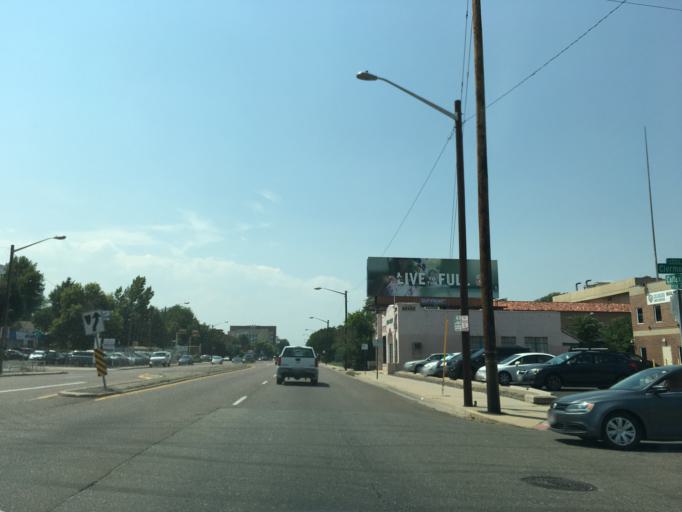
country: US
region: Colorado
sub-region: Arapahoe County
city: Glendale
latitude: 39.7402
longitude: -104.9353
